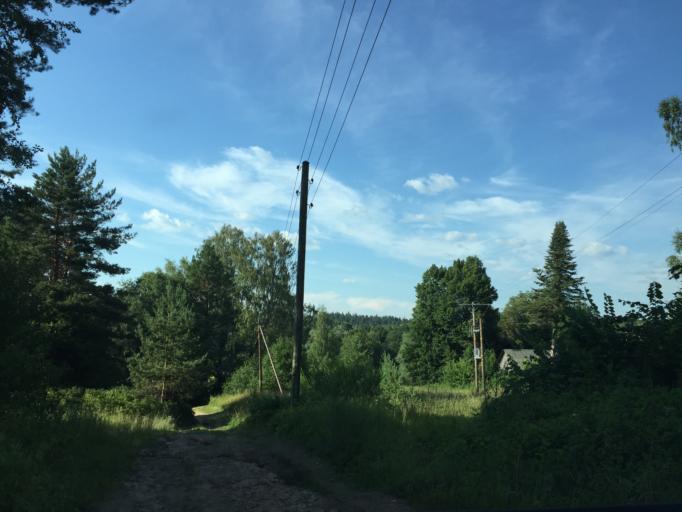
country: LV
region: Krimulda
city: Ragana
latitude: 57.1435
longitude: 24.7642
